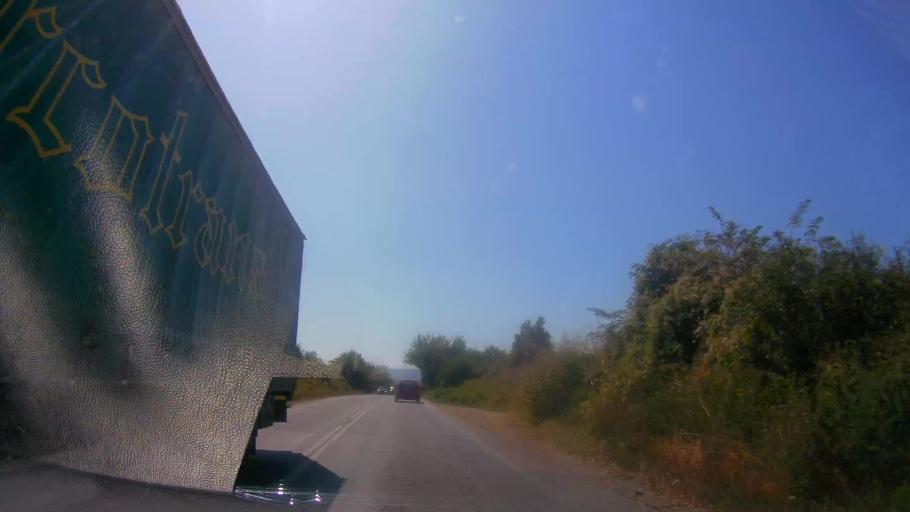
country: BG
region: Veliko Turnovo
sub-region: Obshtina Gorna Oryakhovitsa
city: Purvomaytsi
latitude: 43.2319
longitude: 25.6403
